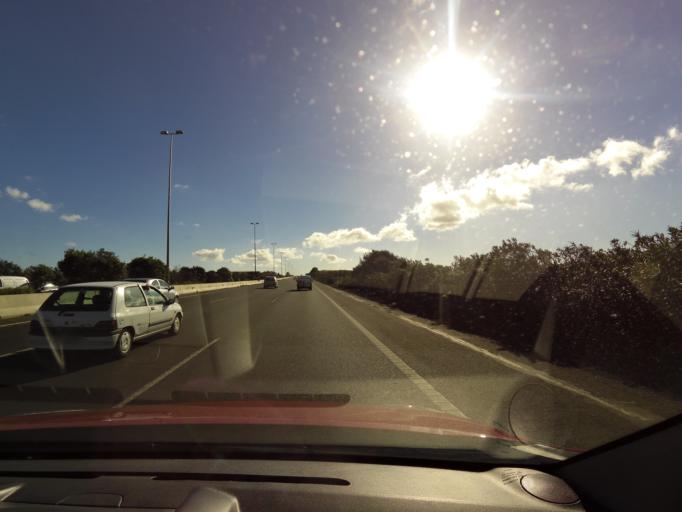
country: ES
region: Canary Islands
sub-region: Provincia de Las Palmas
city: Cruce de Arinaga
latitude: 27.8913
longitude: -15.4080
